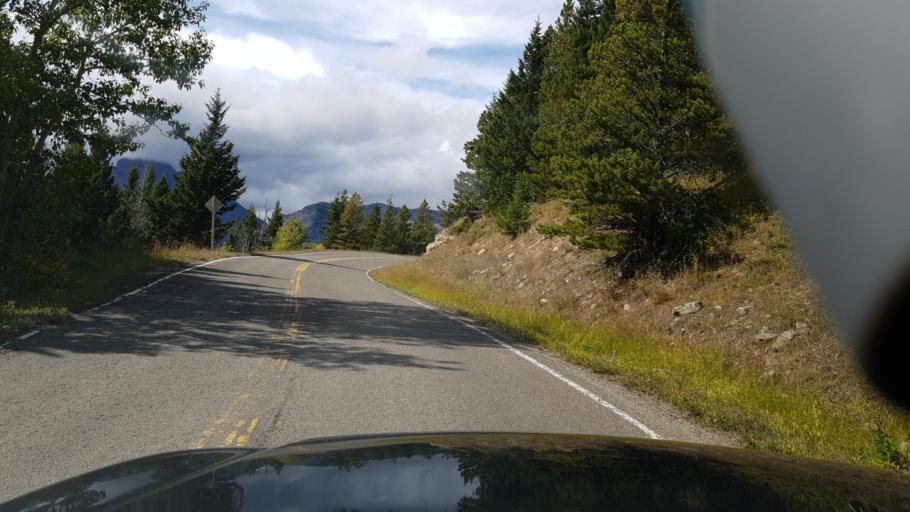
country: US
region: Montana
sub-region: Glacier County
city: South Browning
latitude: 48.5197
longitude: -113.2901
